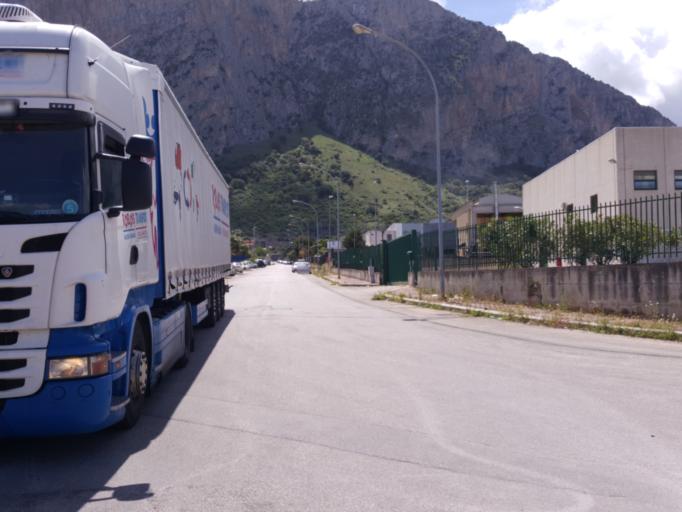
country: IT
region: Sicily
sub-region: Palermo
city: Carini
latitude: 38.1571
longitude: 13.2095
